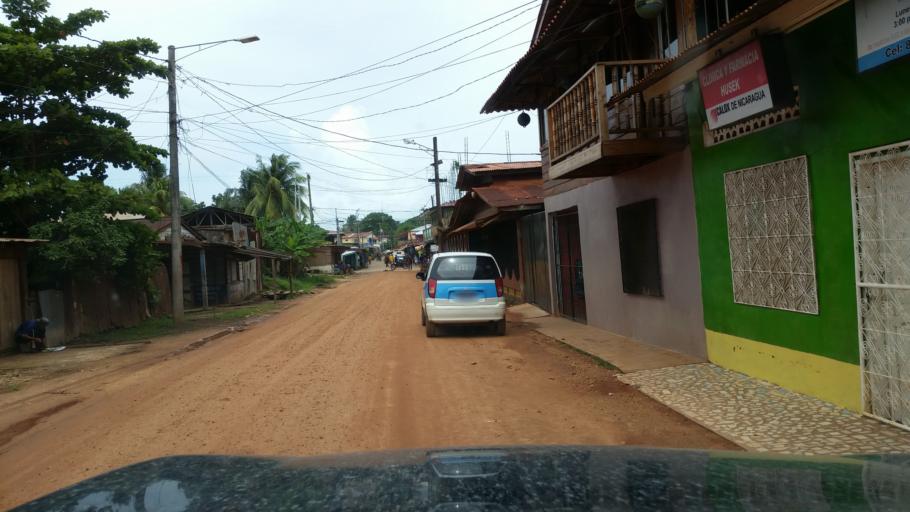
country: NI
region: Atlantico Norte (RAAN)
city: Puerto Cabezas
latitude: 14.0300
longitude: -83.3830
